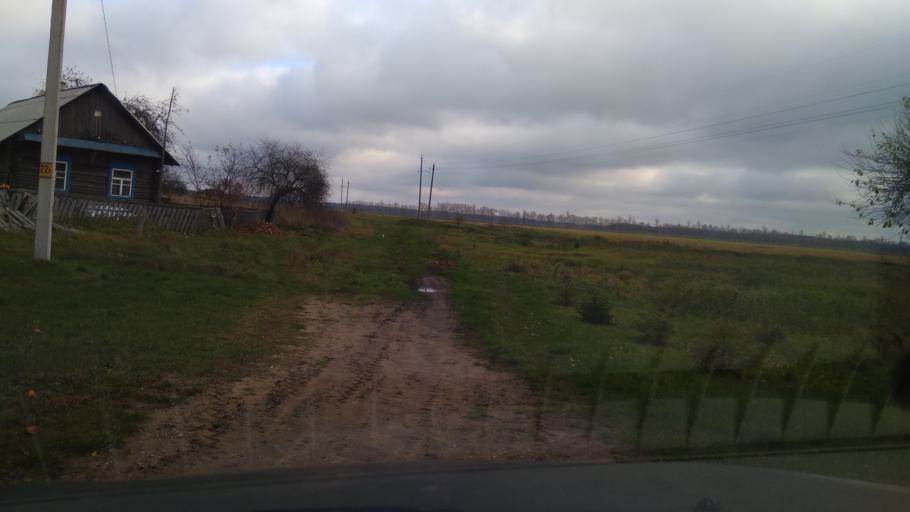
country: BY
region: Minsk
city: Staryya Darohi
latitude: 53.2019
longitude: 28.0457
